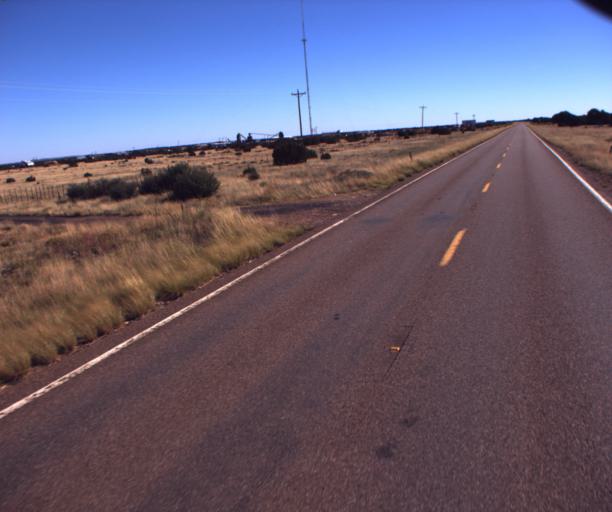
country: US
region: Arizona
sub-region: Navajo County
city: Heber-Overgaard
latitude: 34.4604
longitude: -110.4094
